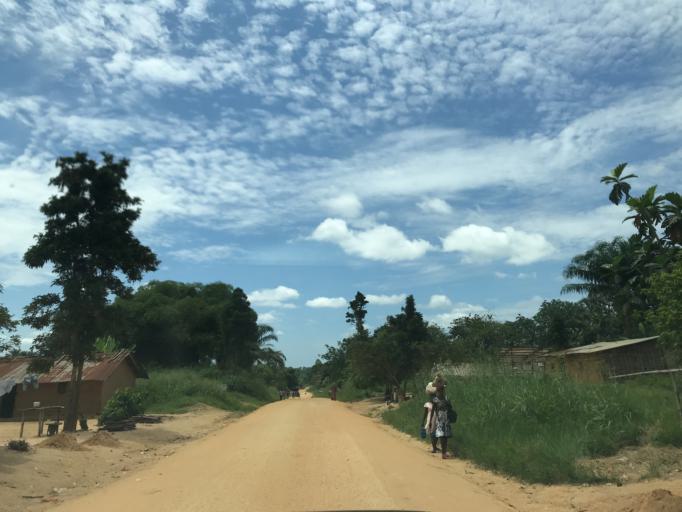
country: CD
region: Eastern Province
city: Kisangani
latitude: 0.5724
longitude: 25.1832
